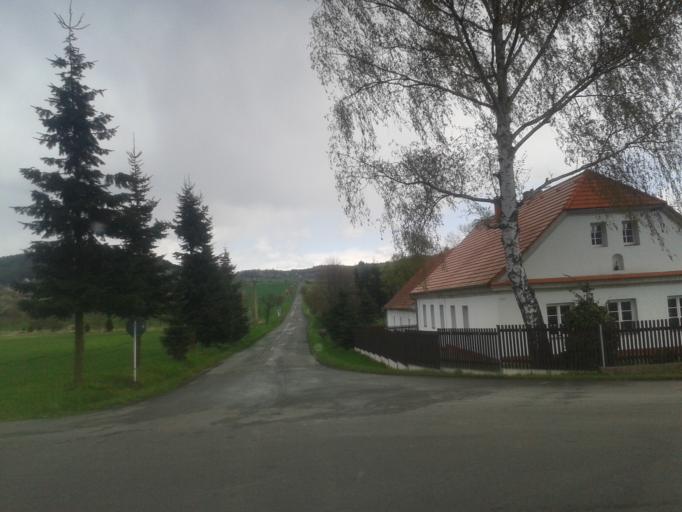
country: CZ
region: Central Bohemia
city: Zebrak
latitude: 49.9327
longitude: 13.8653
